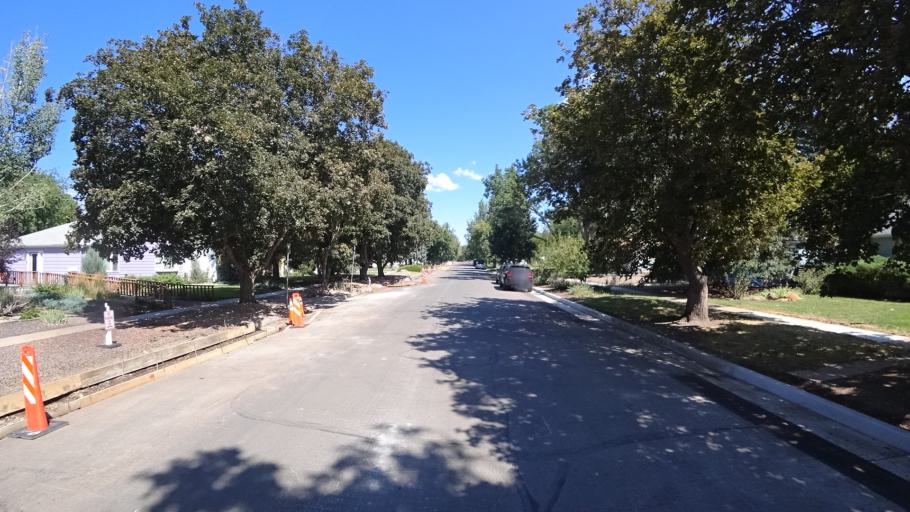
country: US
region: Colorado
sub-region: El Paso County
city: Colorado Springs
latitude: 38.8659
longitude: -104.8126
